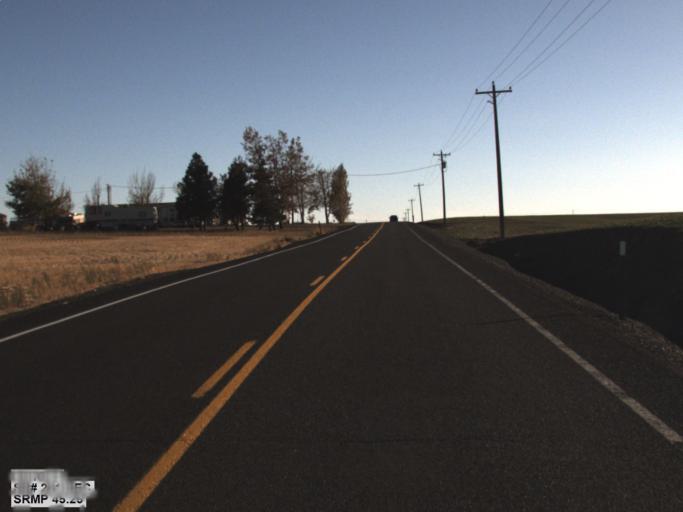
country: US
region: Washington
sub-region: Adams County
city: Ritzville
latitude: 46.8748
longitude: -118.3354
